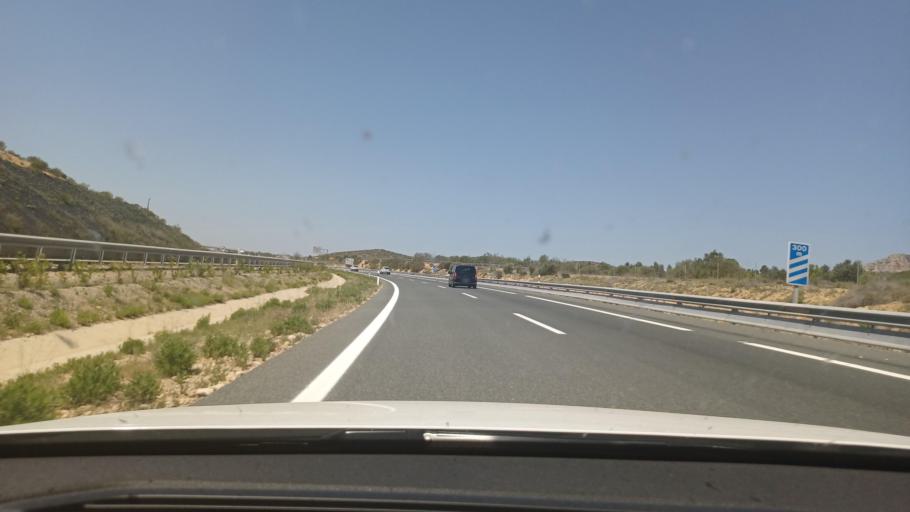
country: ES
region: Castille-La Mancha
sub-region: Provincia de Albacete
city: Almansa
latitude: 38.8795
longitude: -1.1626
